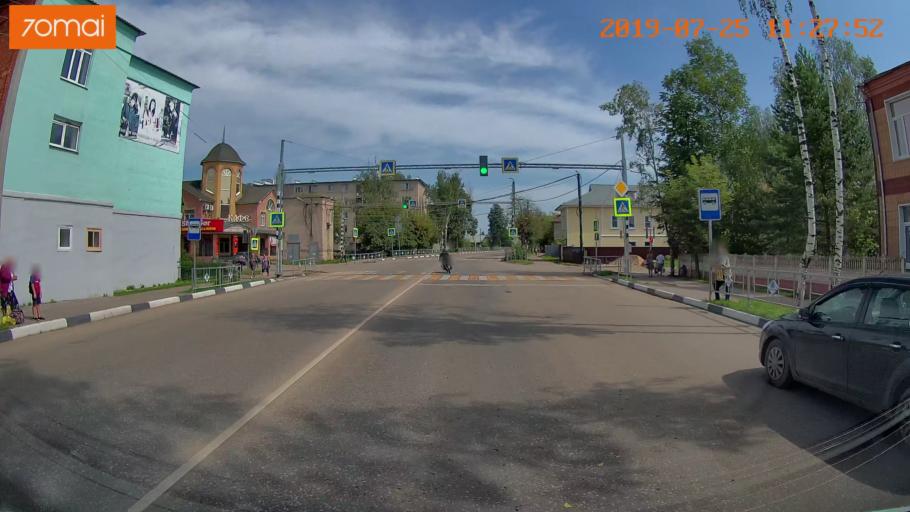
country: RU
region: Ivanovo
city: Privolzhsk
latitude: 57.3786
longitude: 41.2880
